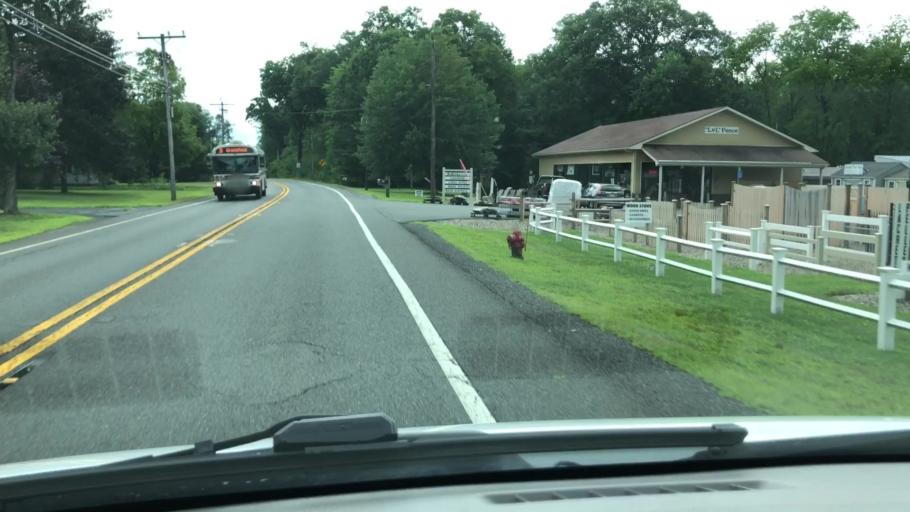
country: US
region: Massachusetts
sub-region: Franklin County
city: Whately
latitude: 42.4218
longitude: -72.6222
